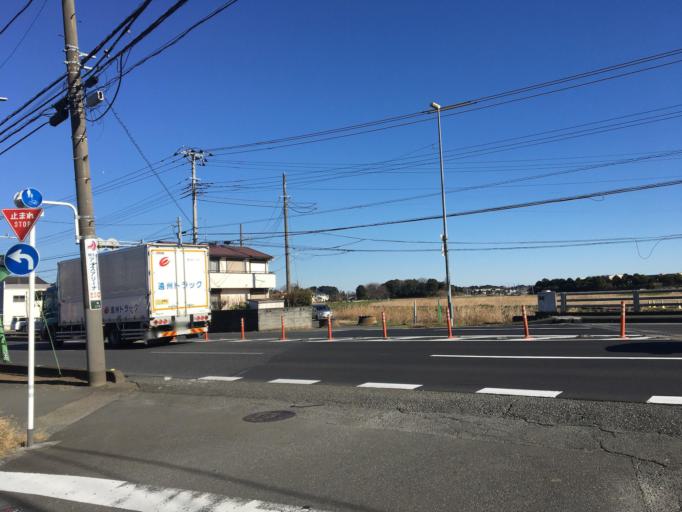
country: JP
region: Saitama
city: Hasuda
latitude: 35.9709
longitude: 139.6352
